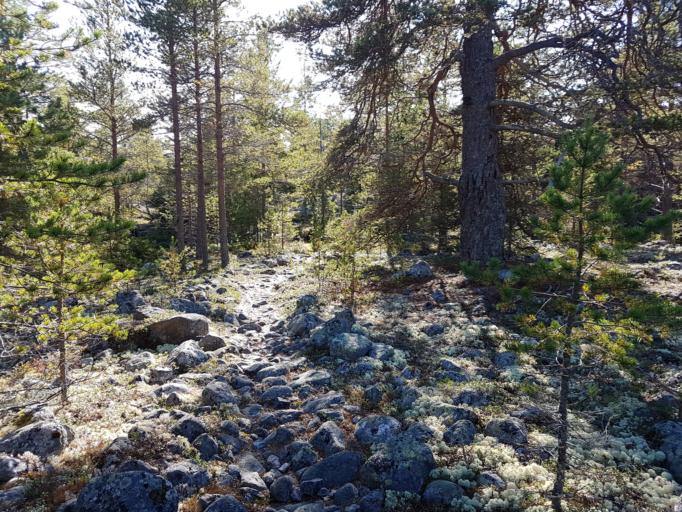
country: SE
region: Vaesterbotten
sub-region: Skelleftea Kommun
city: Skelleftehamn
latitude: 64.4780
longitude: 21.5777
